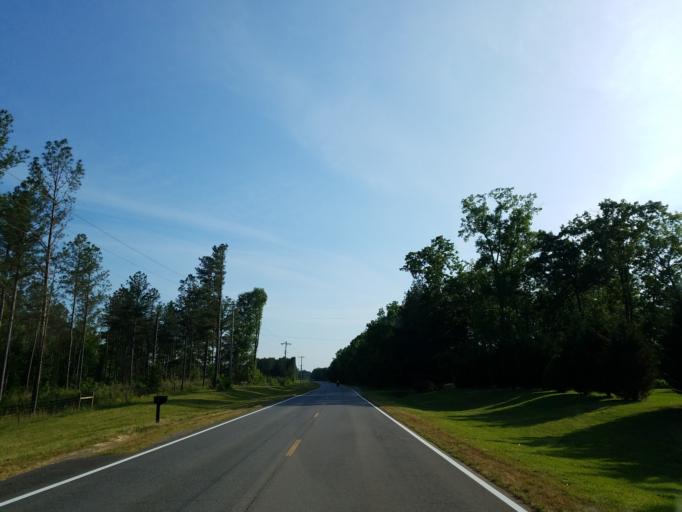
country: US
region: Georgia
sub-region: Chattooga County
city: Trion
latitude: 34.5302
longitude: -85.2127
